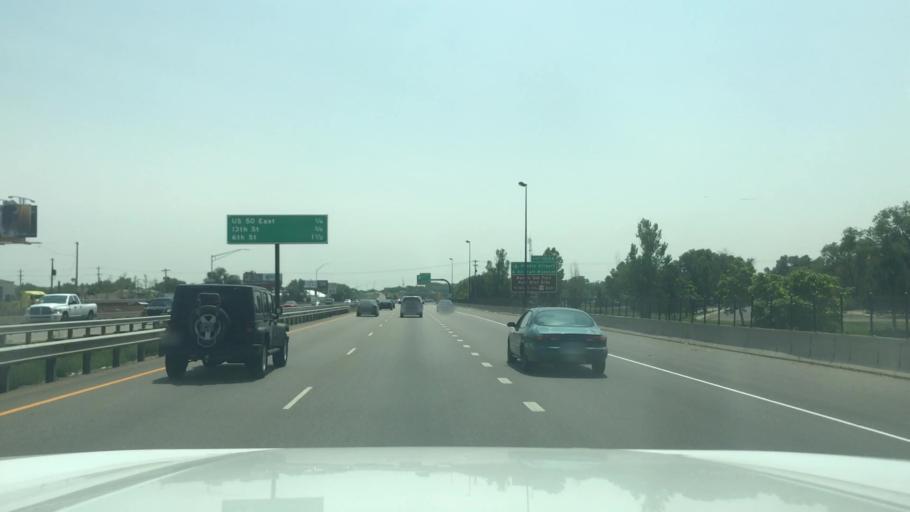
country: US
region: Colorado
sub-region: Pueblo County
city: Pueblo
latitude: 38.2935
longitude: -104.6090
